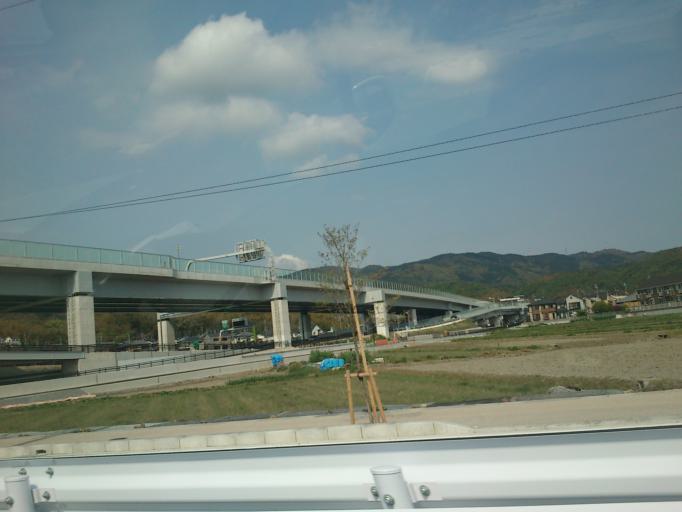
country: JP
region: Kyoto
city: Yawata
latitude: 34.9159
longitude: 135.6875
